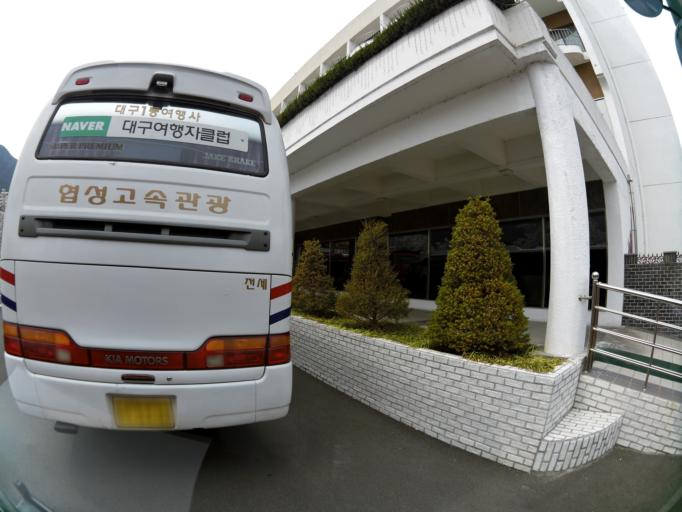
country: KR
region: Gyeongsangnam-do
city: Changnyeong
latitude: 35.4384
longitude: 128.5924
